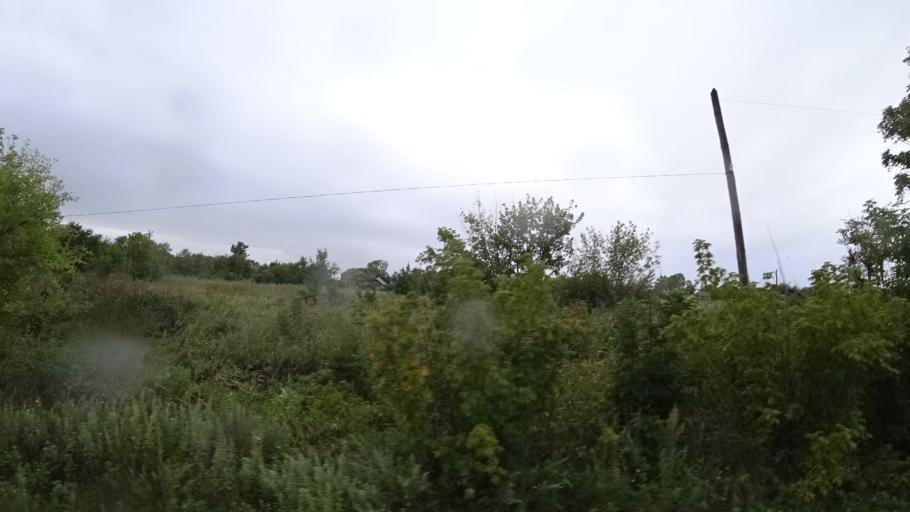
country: RU
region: Primorskiy
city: Chernigovka
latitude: 44.4060
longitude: 132.5297
